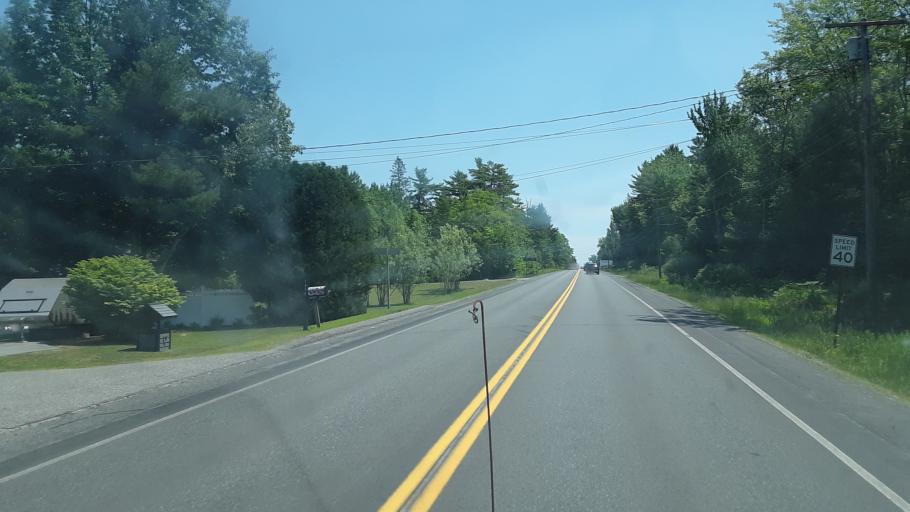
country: US
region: Maine
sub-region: Hancock County
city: Hancock
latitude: 44.5277
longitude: -68.2508
